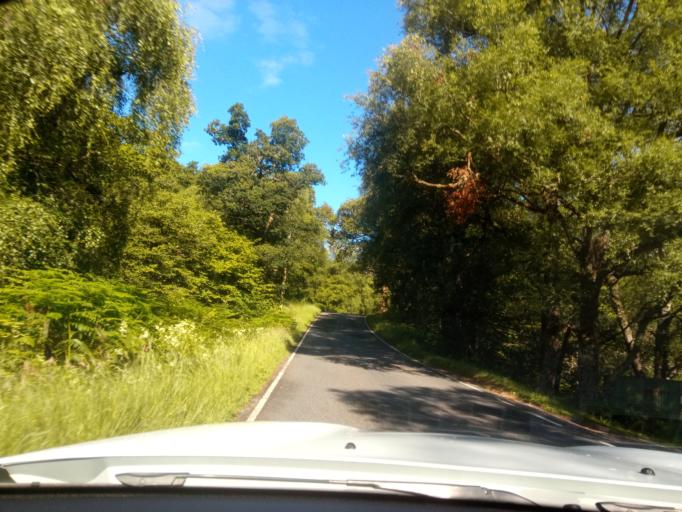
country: GB
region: Scotland
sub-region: Argyll and Bute
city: Isle Of Mull
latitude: 56.6919
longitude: -5.6686
